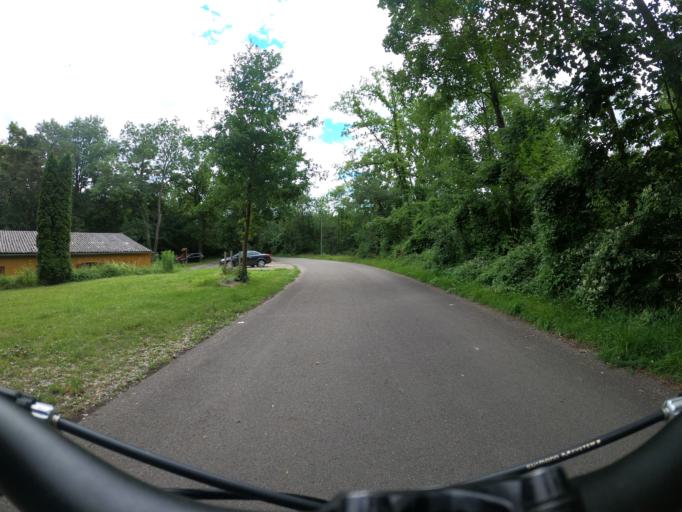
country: DE
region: Bavaria
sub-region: Swabia
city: Nersingen
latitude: 48.4371
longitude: 10.1064
